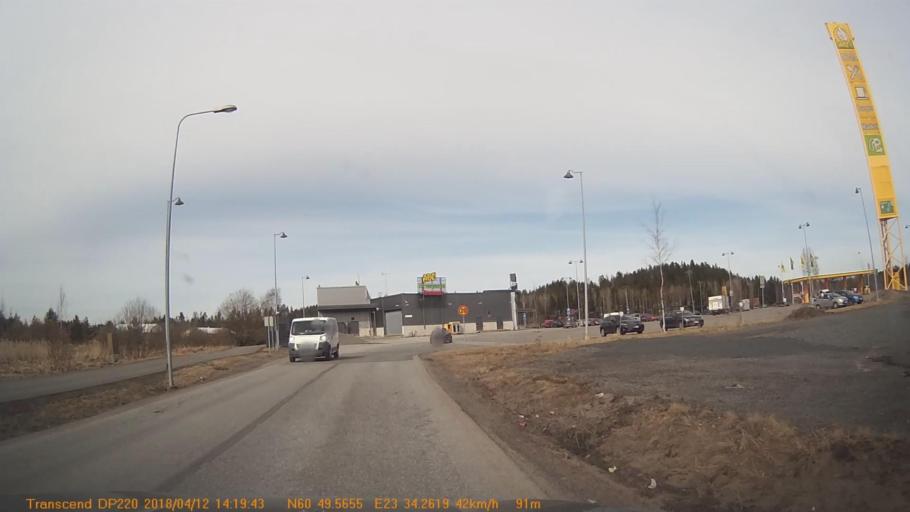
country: FI
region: Haeme
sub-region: Forssa
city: Forssa
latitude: 60.8241
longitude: 23.5654
